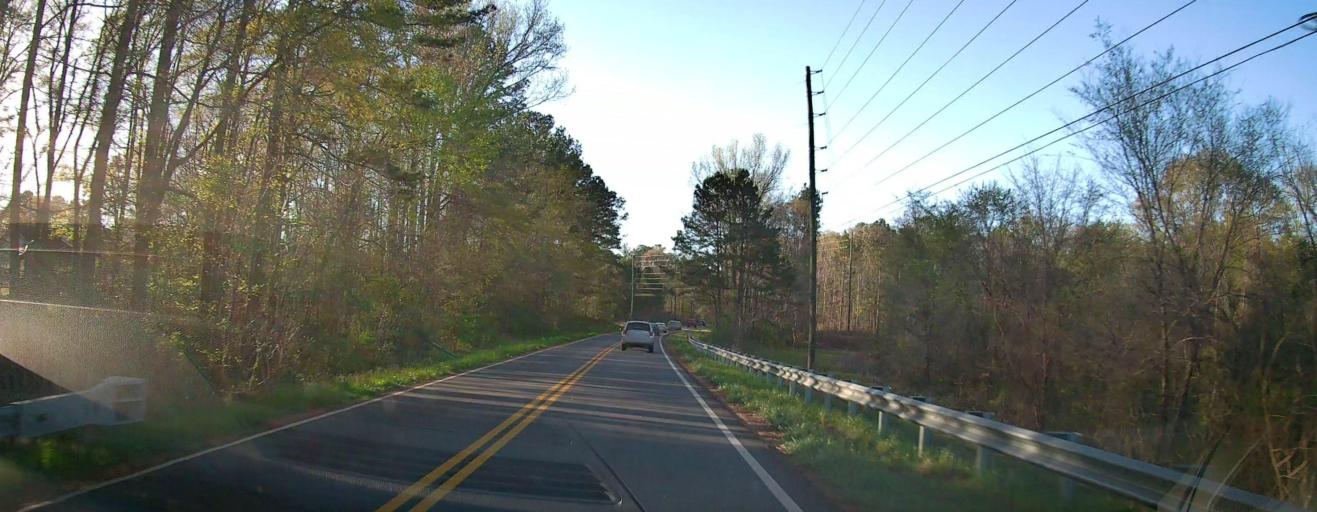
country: US
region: Georgia
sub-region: Newton County
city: Porterdale
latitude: 33.5772
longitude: -83.9055
